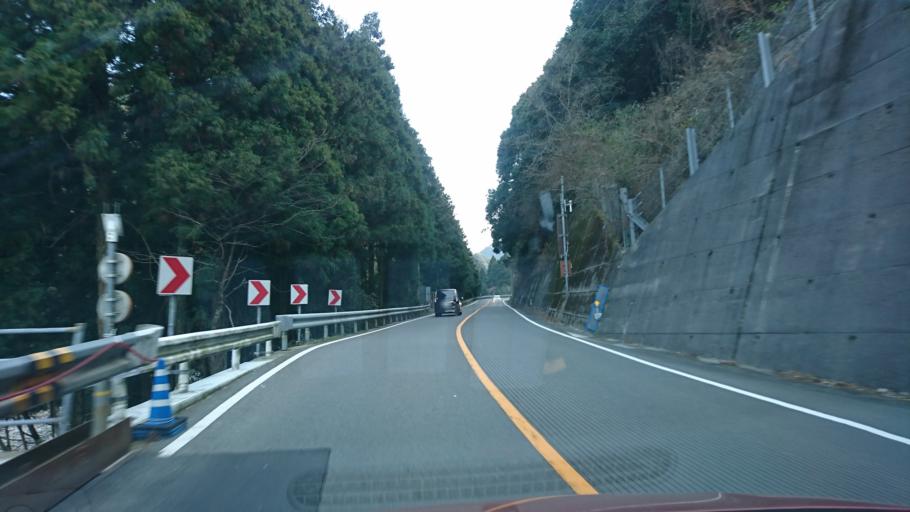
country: JP
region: Ehime
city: Hojo
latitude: 33.9666
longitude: 132.9050
